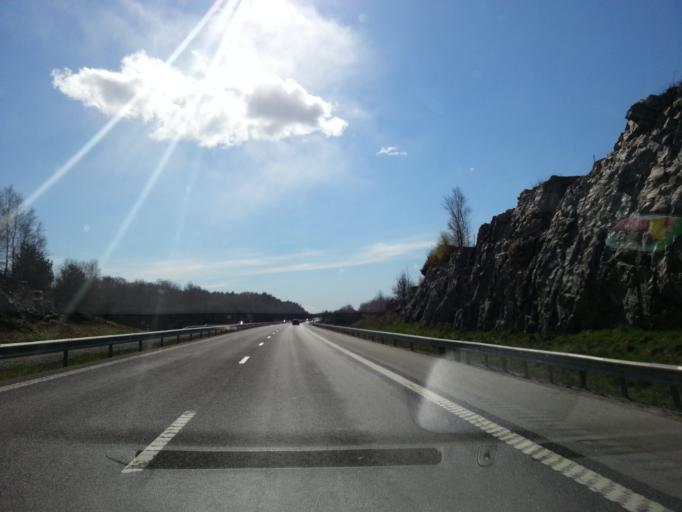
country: SE
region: Vaestra Goetaland
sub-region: Stenungsunds Kommun
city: Stora Hoga
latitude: 58.0527
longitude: 11.8691
